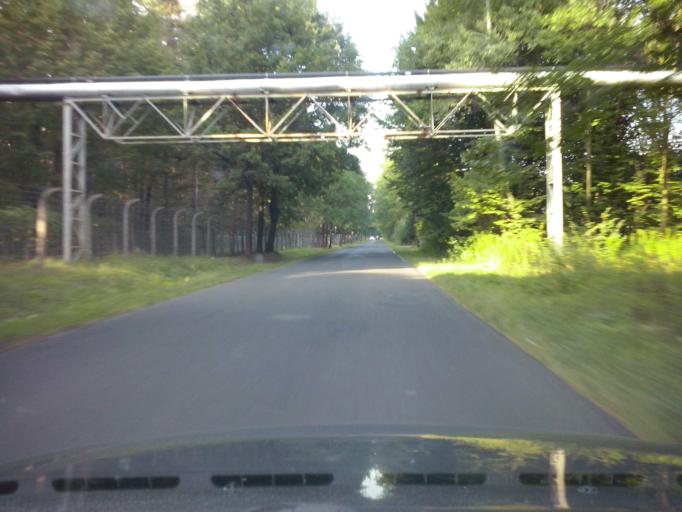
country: PL
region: Subcarpathian Voivodeship
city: Nowa Sarzyna
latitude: 50.3201
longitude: 22.3317
